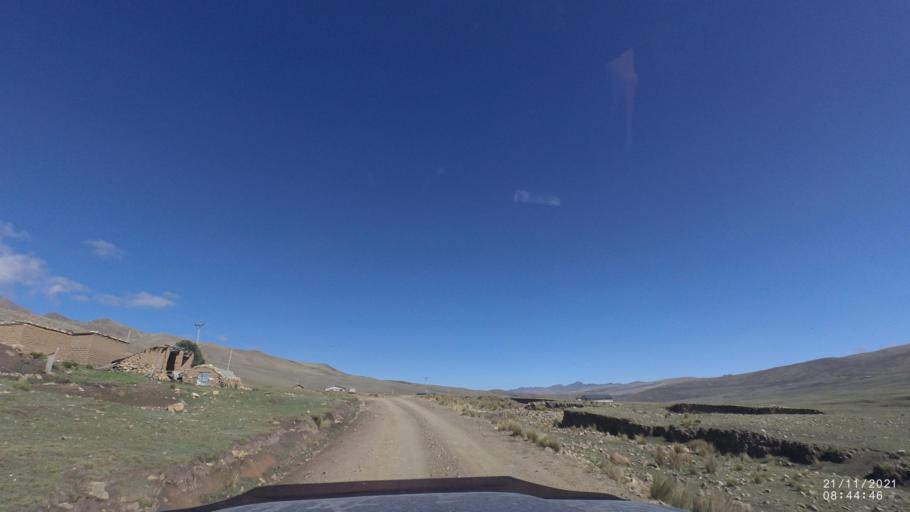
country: BO
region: Cochabamba
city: Cochabamba
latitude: -17.2515
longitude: -66.2289
